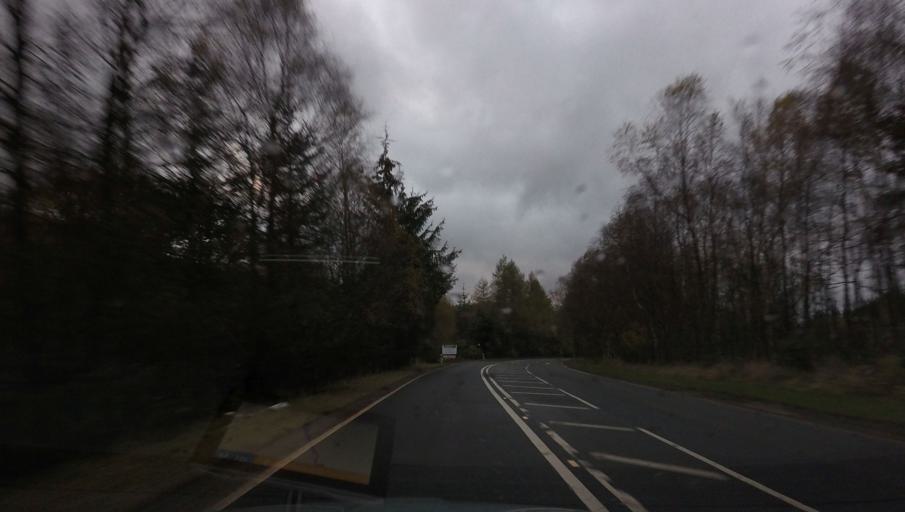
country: GB
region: Scotland
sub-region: Stirling
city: Callander
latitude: 56.3614
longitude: -4.3064
